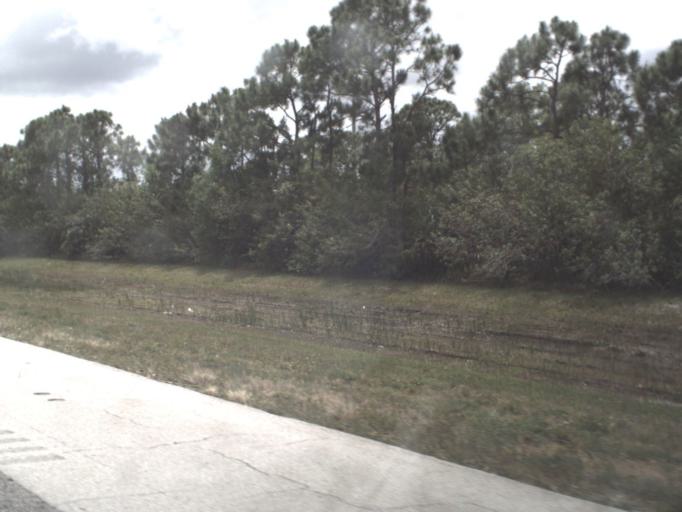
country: US
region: Florida
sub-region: Brevard County
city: June Park
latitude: 28.1565
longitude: -80.7061
